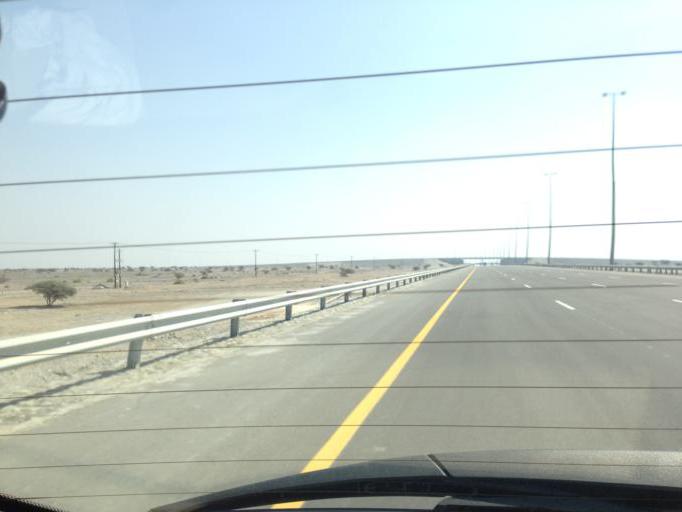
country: OM
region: Al Batinah
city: Barka'
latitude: 23.5758
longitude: 57.7625
